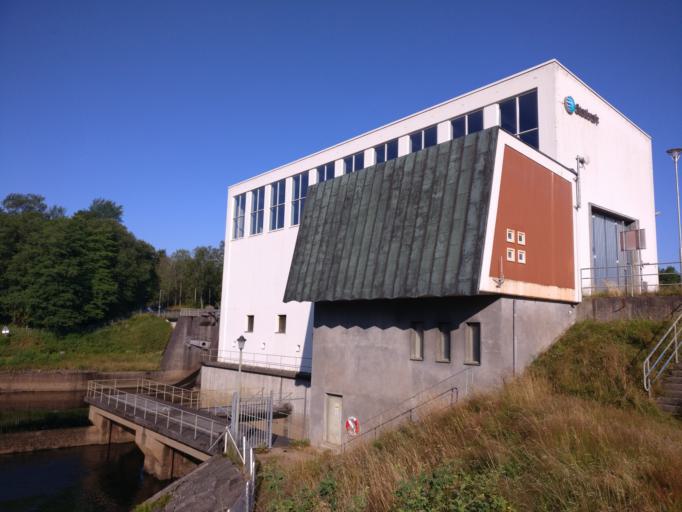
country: SE
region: Kronoberg
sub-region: Markaryds Kommun
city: Stromsnasbruk
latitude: 56.5384
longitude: 13.7129
